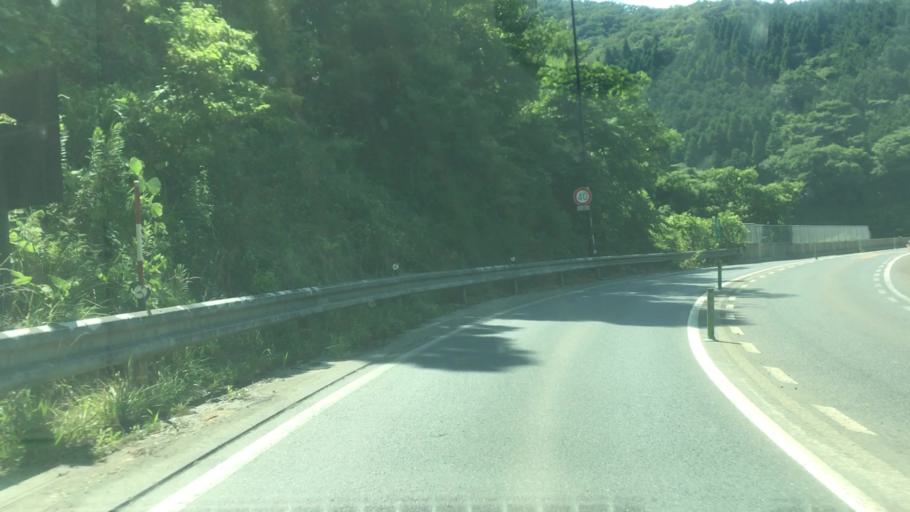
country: JP
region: Tottori
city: Tottori
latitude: 35.2768
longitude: 134.2261
